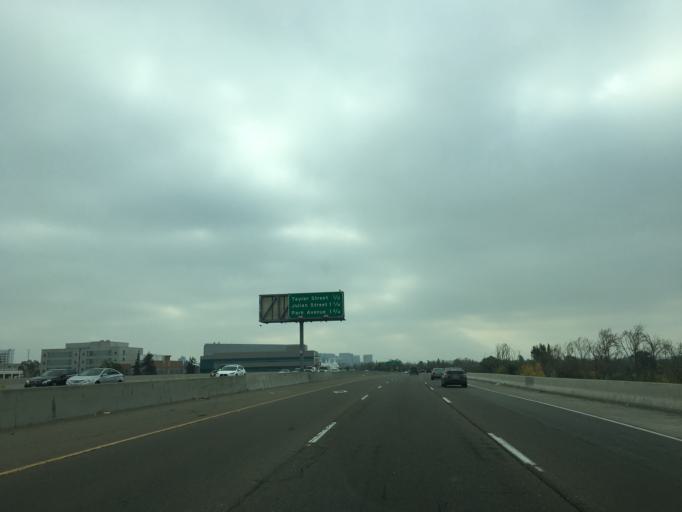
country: US
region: California
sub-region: Santa Clara County
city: San Jose
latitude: 37.3530
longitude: -121.9108
